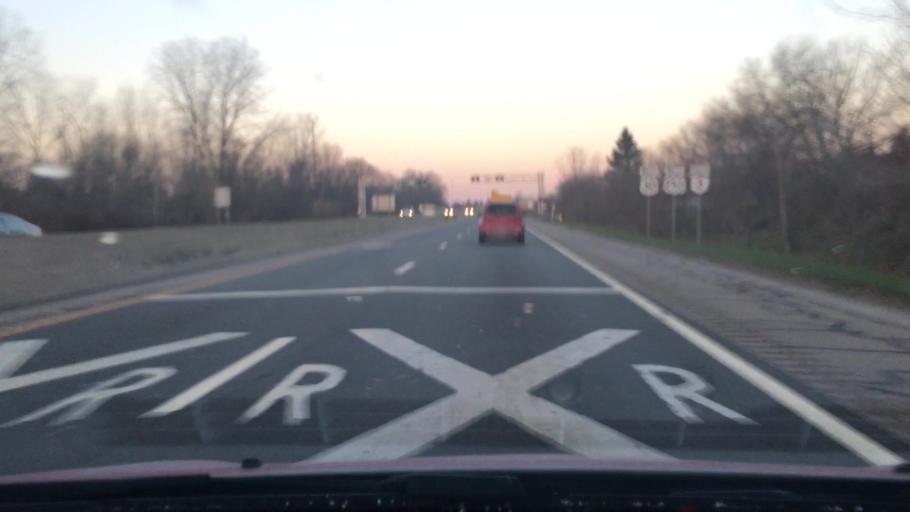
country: US
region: Ohio
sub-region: Wayne County
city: Wooster
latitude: 40.7918
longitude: -81.9404
